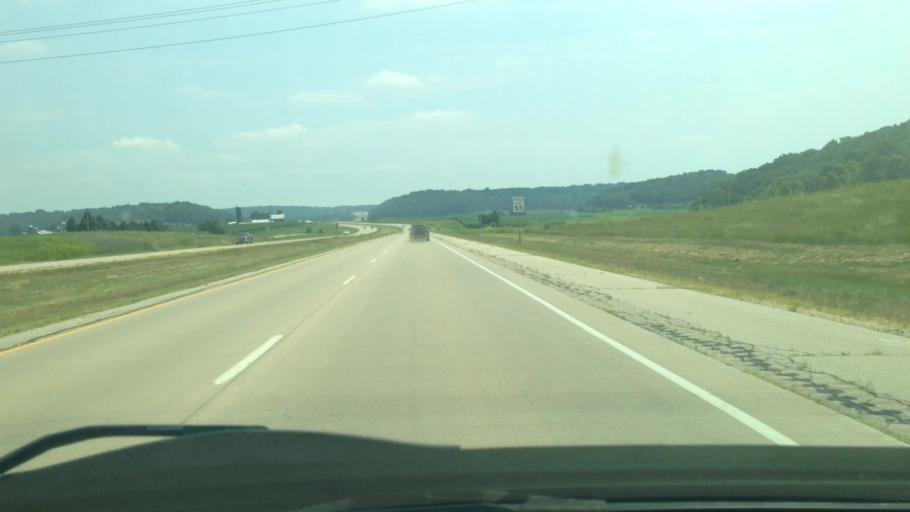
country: US
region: Wisconsin
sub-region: Sauk County
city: Sauk City
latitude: 43.2223
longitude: -89.6594
